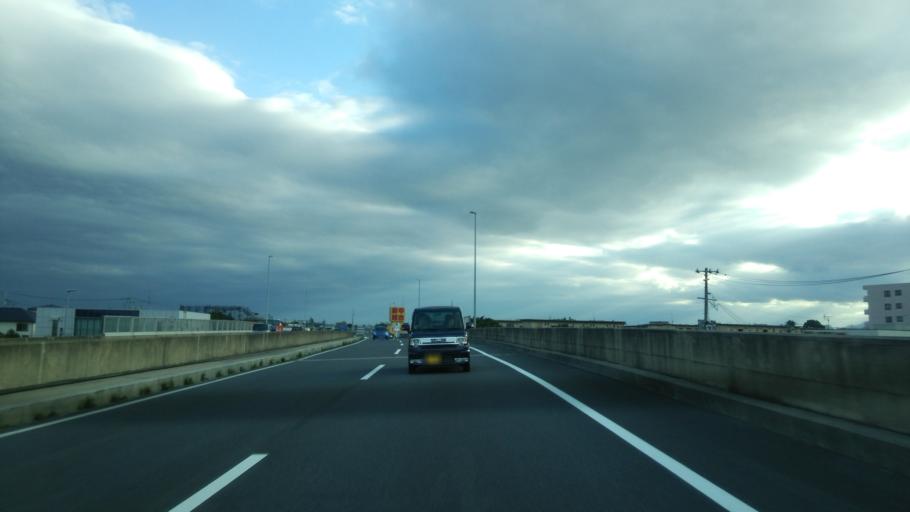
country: JP
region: Fukushima
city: Koriyama
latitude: 37.4085
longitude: 140.3438
